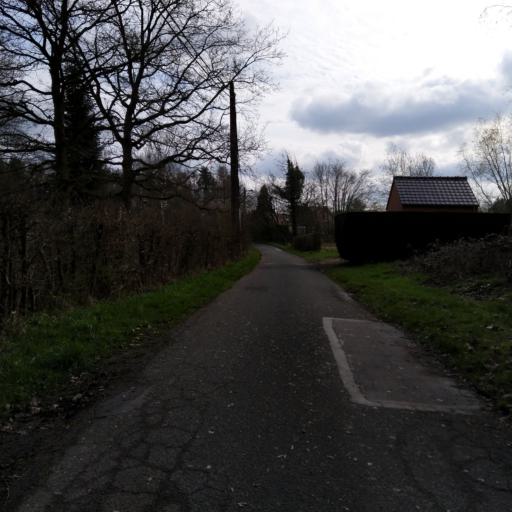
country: BE
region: Wallonia
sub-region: Province du Hainaut
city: Mons
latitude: 50.5135
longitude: 3.9977
